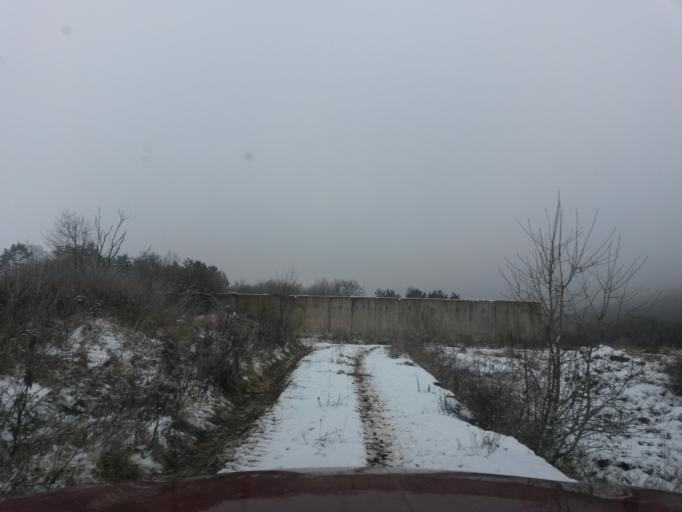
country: SK
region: Presovsky
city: Sabinov
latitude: 48.9570
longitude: 21.0900
